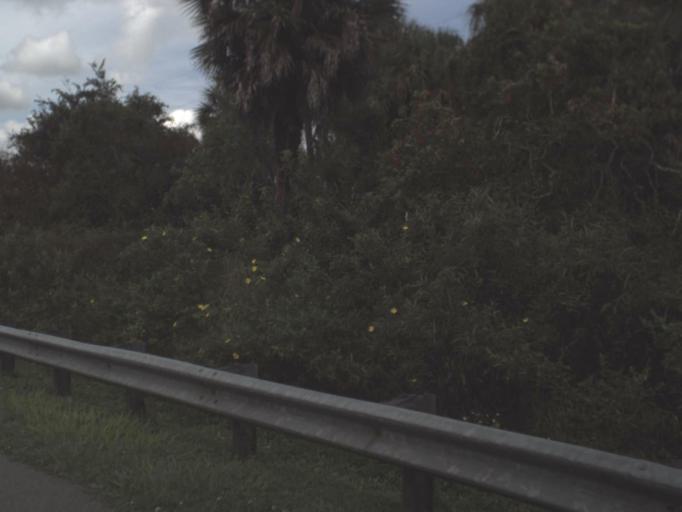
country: US
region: Florida
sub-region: Highlands County
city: Lake Placid
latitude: 27.2099
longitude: -81.1389
